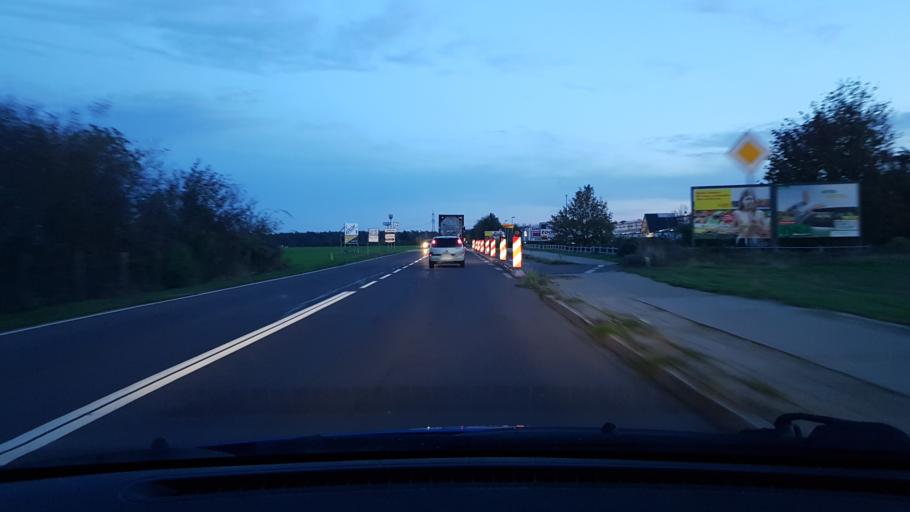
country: DE
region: Saxony-Anhalt
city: Zerbst
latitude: 51.9543
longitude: 12.1032
